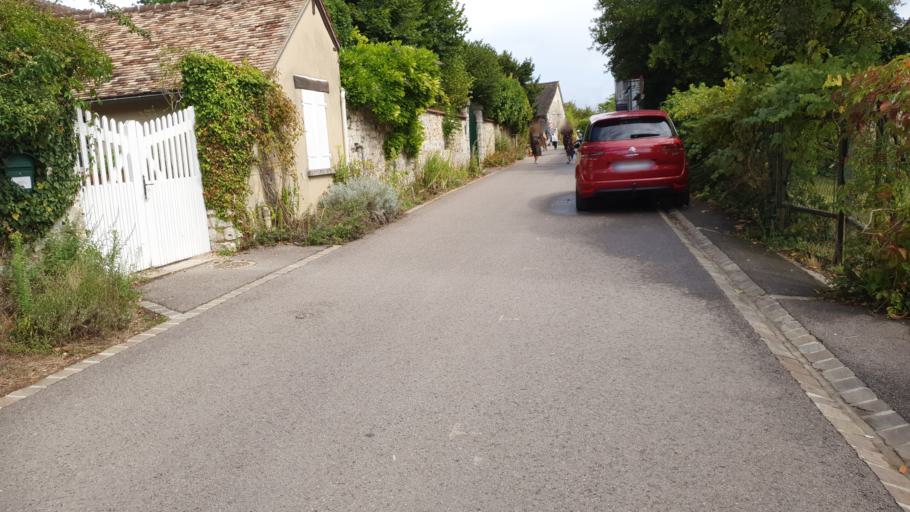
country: FR
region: Ile-de-France
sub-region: Departement des Yvelines
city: Limetz-Villez
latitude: 49.0768
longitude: 1.5282
